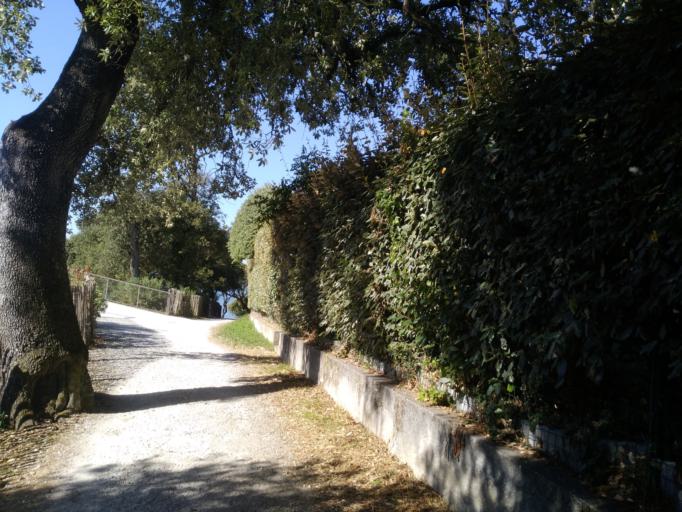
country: FR
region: Poitou-Charentes
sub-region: Departement de la Charente-Maritime
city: Saint-Palais-sur-Mer
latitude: 45.6406
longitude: -1.0916
